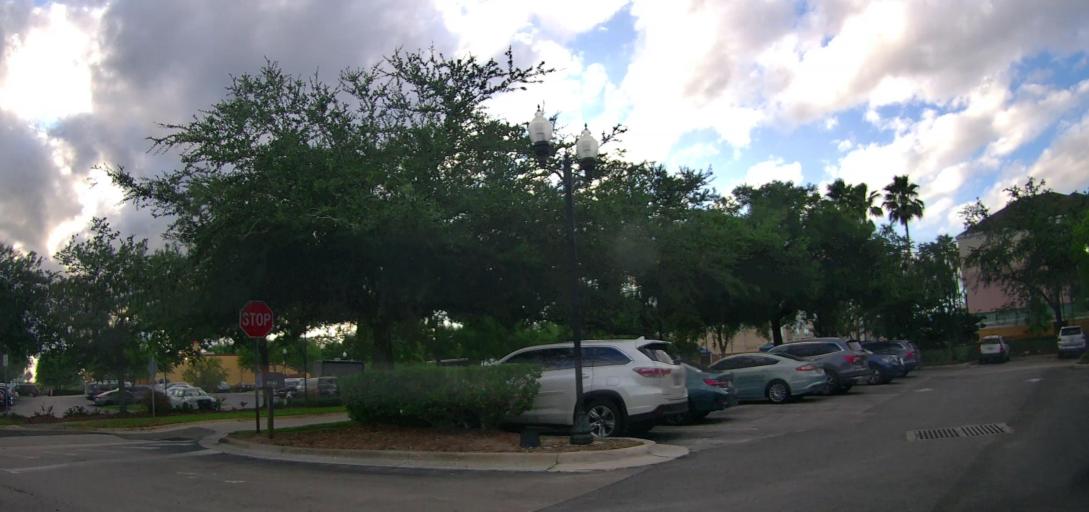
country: US
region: Florida
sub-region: Osceola County
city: Celebration
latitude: 28.3755
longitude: -81.5023
